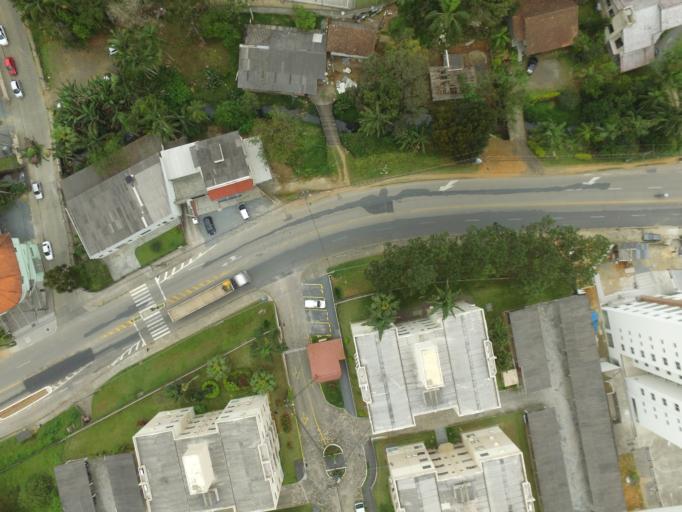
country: BR
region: Santa Catarina
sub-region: Blumenau
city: Blumenau
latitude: -26.8941
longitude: -49.1309
